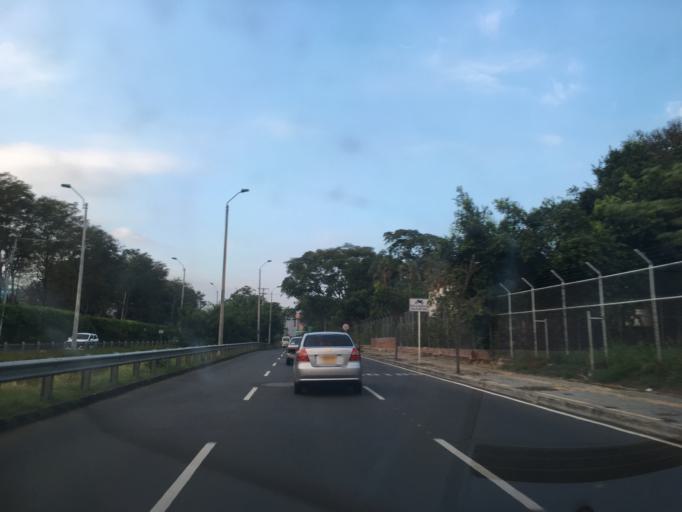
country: CO
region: Valle del Cauca
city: Cali
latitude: 3.3732
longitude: -76.5294
